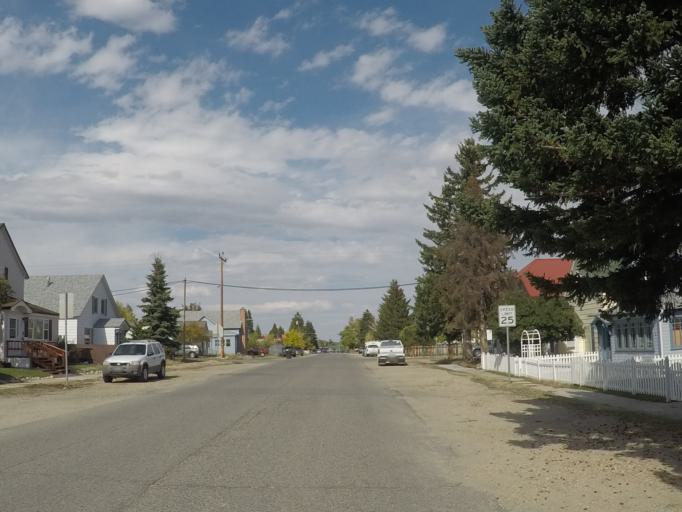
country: US
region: Montana
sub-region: Carbon County
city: Red Lodge
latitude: 45.1824
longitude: -109.2482
